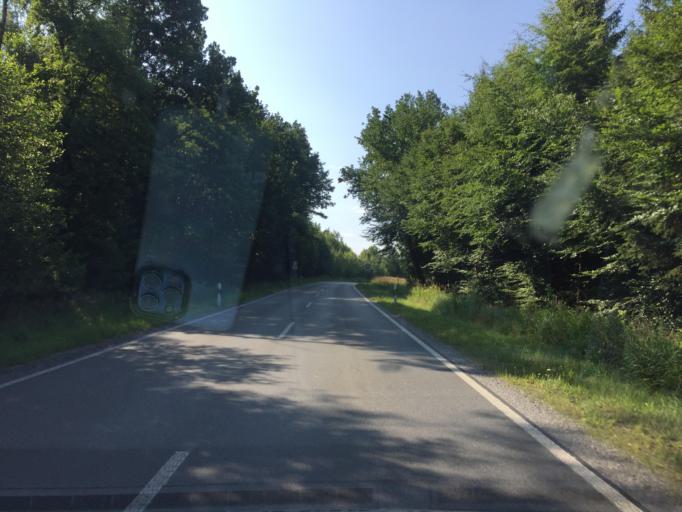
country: DE
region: Bavaria
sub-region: Upper Bavaria
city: Tuntenhausen
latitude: 47.9105
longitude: 11.9889
